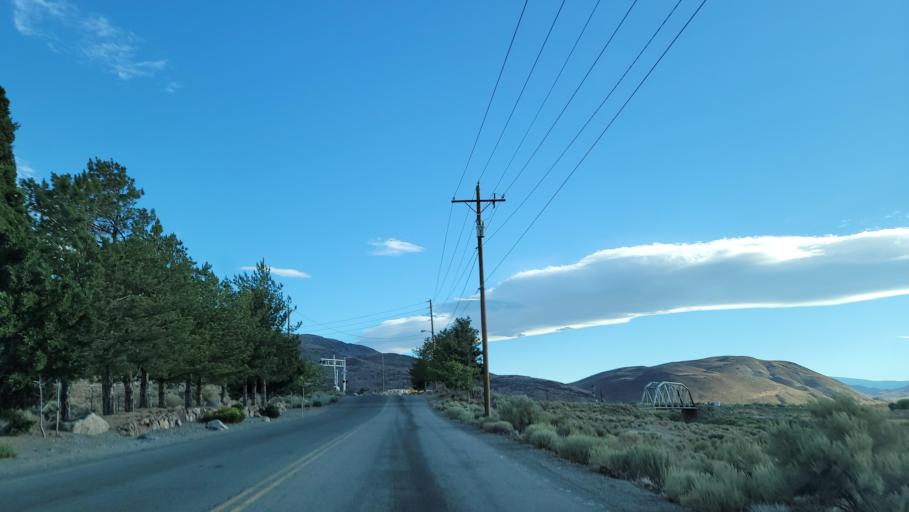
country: US
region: Nevada
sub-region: Washoe County
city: Spanish Springs
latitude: 39.5552
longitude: -119.5530
